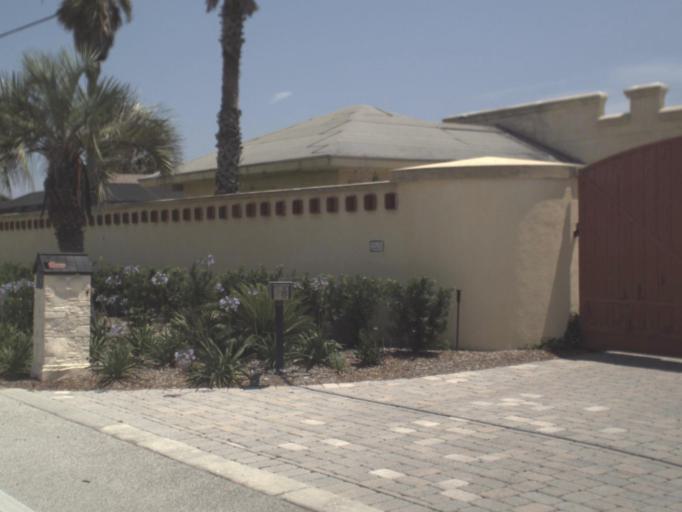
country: US
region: Florida
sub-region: Saint Johns County
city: Villano Beach
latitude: 30.0468
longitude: -81.3294
